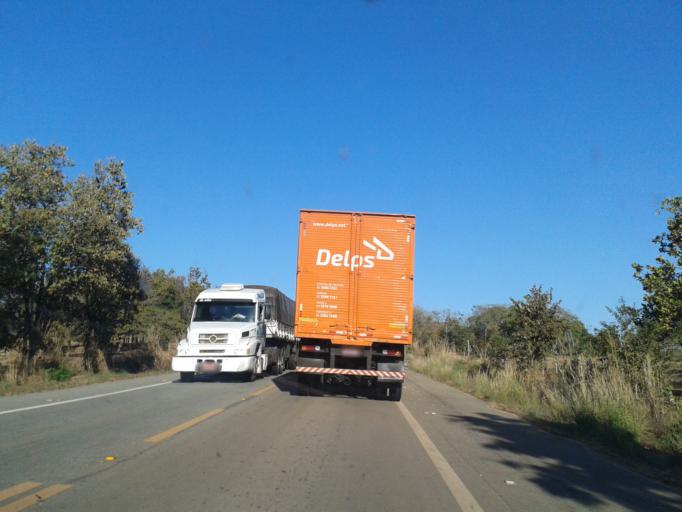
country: BR
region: Goias
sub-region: Itapirapua
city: Itapirapua
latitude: -15.3174
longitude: -50.4401
